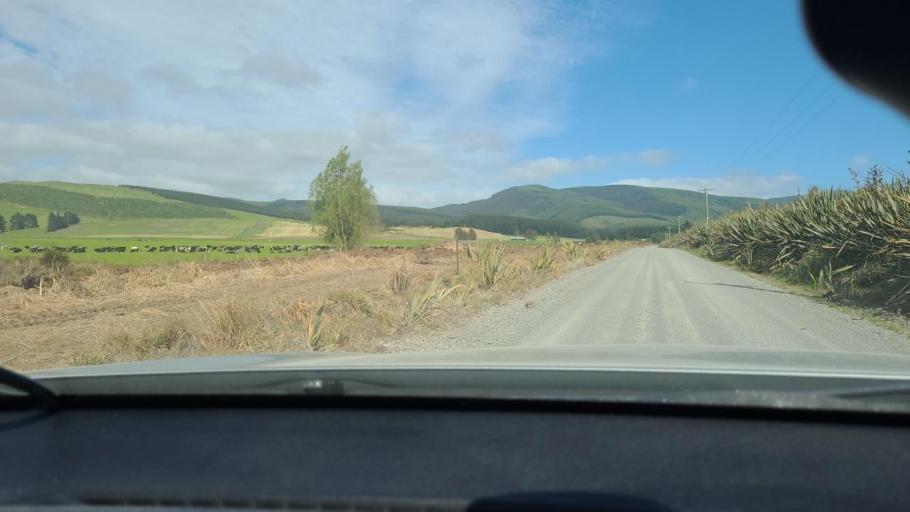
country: NZ
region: Southland
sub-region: Southland District
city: Winton
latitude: -45.8970
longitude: 168.1051
